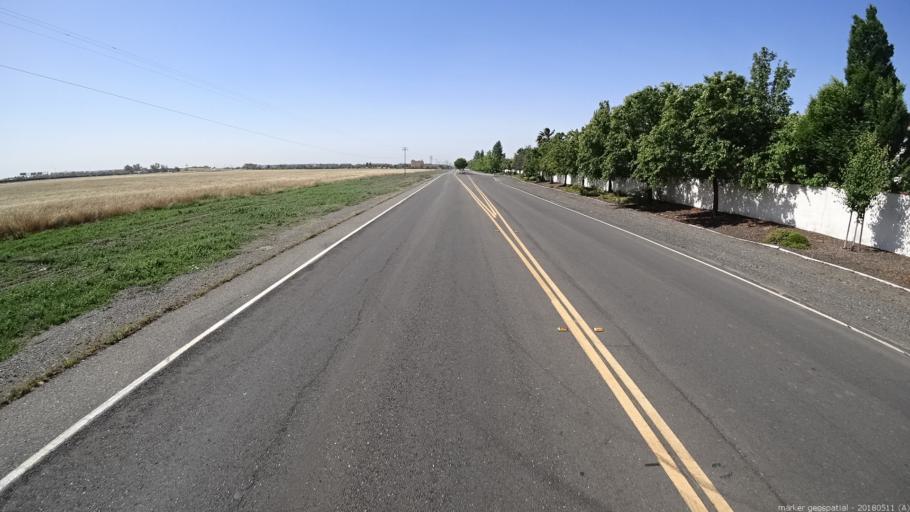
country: US
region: California
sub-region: Yolo County
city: West Sacramento
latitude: 38.6616
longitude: -121.5399
